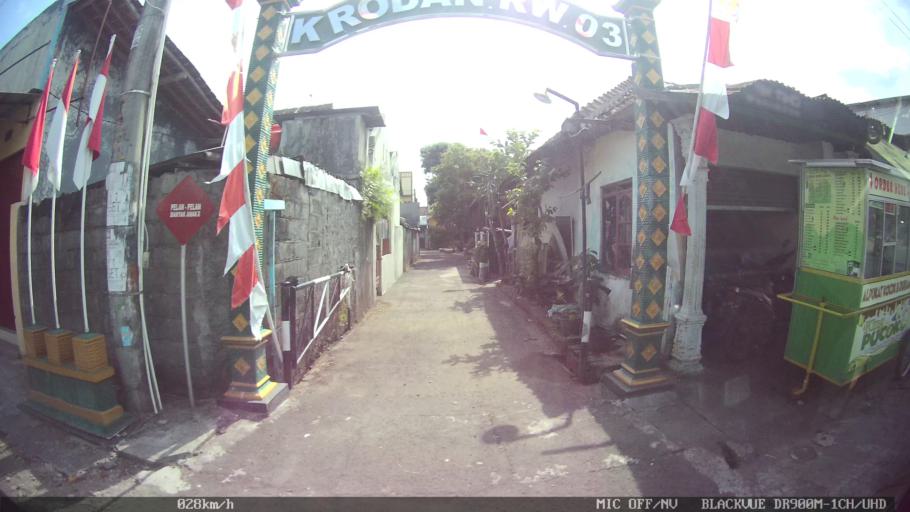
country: ID
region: Daerah Istimewa Yogyakarta
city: Depok
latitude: -7.7576
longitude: 110.4229
